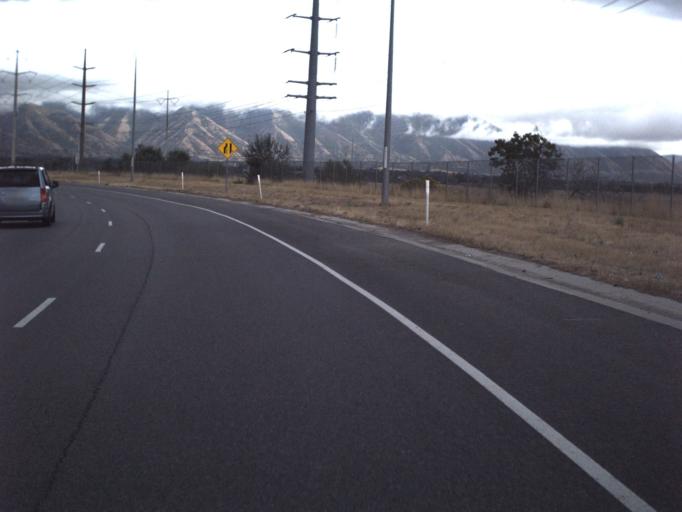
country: US
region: Utah
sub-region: Utah County
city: Provo
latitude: 40.2047
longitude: -111.6598
